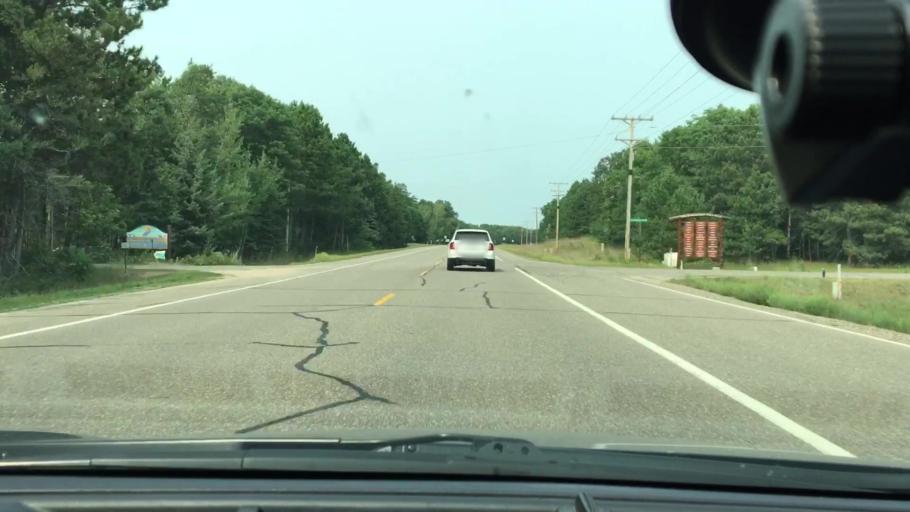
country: US
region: Minnesota
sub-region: Crow Wing County
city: Cross Lake
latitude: 46.5916
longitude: -94.1316
